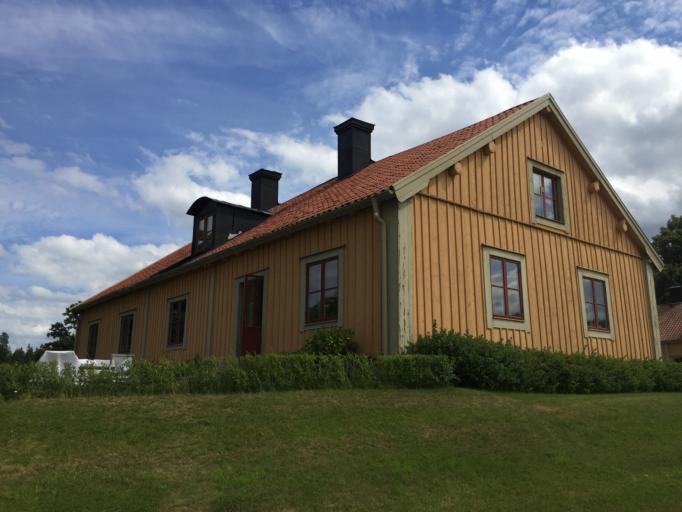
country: SE
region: Soedermanland
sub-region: Strangnas Kommun
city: Akers Styckebruk
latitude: 59.2508
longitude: 16.9345
